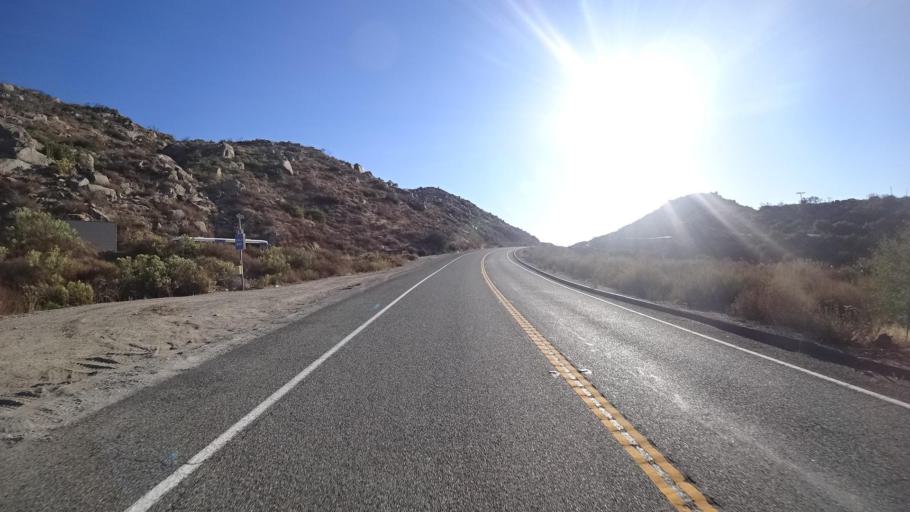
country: MX
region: Baja California
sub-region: Tecate
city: Hacienda Tecate
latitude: 32.5992
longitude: -116.5664
